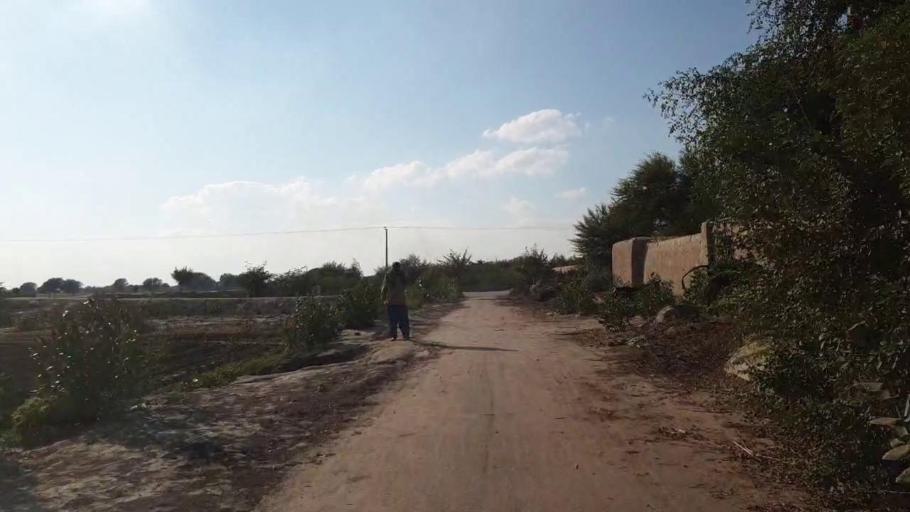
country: PK
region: Sindh
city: Shahpur Chakar
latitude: 26.1058
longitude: 68.5834
